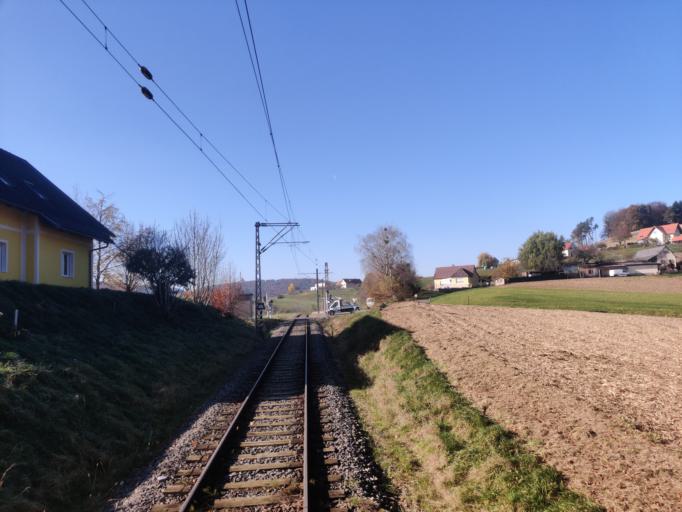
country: AT
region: Styria
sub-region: Politischer Bezirk Suedoststeiermark
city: Trautmannsdorf in Oststeiermark
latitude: 46.8780
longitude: 15.8899
